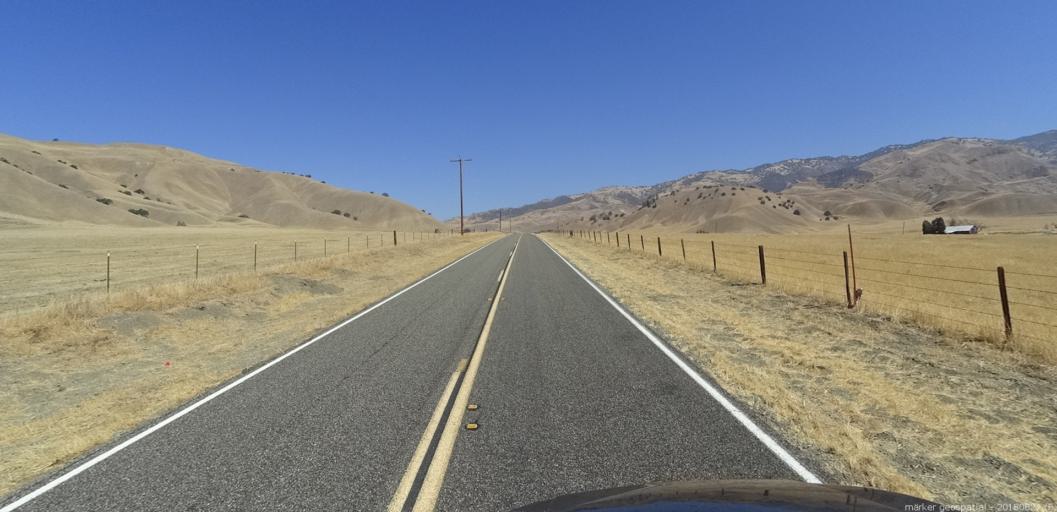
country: US
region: California
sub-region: Monterey County
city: King City
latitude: 36.3060
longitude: -120.9289
